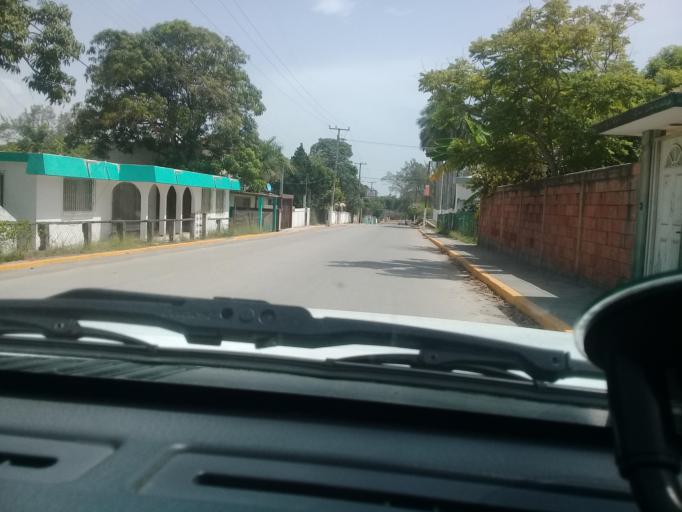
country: MX
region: Veracruz
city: Anahuac
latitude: 22.2265
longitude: -97.8317
